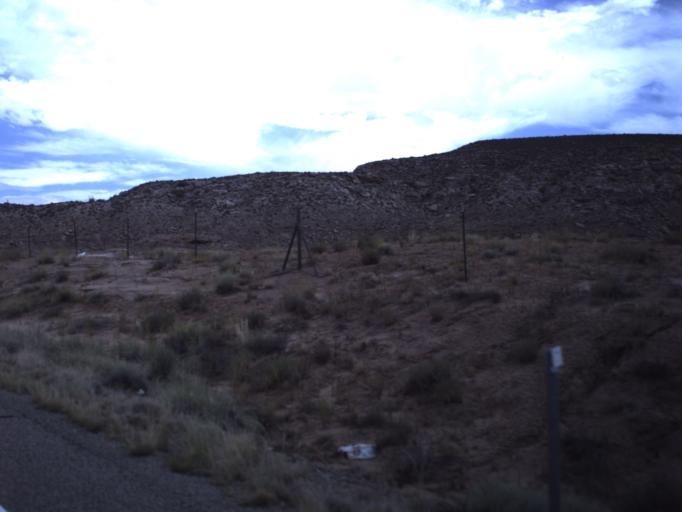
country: US
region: Utah
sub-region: San Juan County
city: Blanding
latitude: 37.2864
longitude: -109.3891
